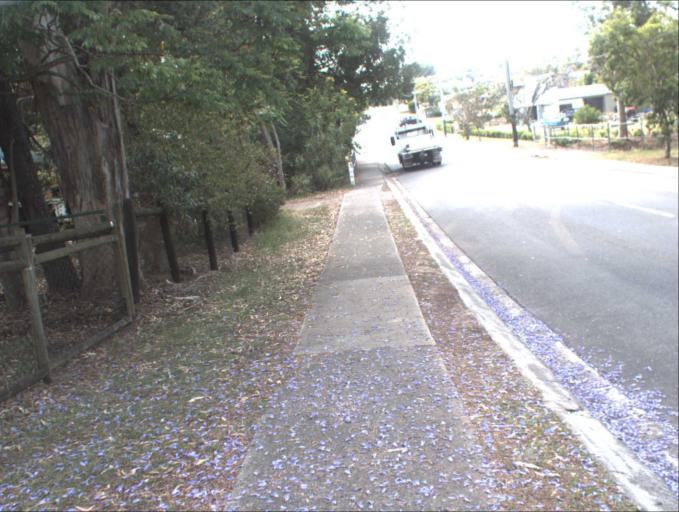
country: AU
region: Queensland
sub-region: Logan
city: Slacks Creek
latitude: -27.6446
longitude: 153.1588
